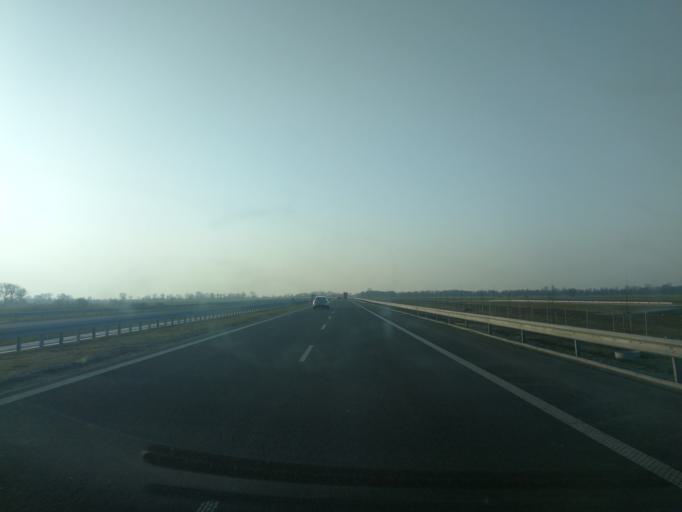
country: PL
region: Warmian-Masurian Voivodeship
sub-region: Powiat elblaski
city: Gronowo Elblaskie
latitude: 54.1690
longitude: 19.2286
